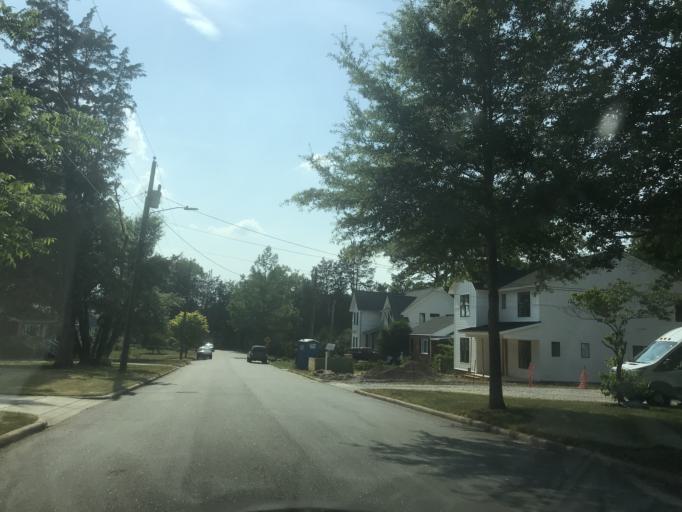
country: US
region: North Carolina
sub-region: Wake County
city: Raleigh
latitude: 35.7881
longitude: -78.6218
